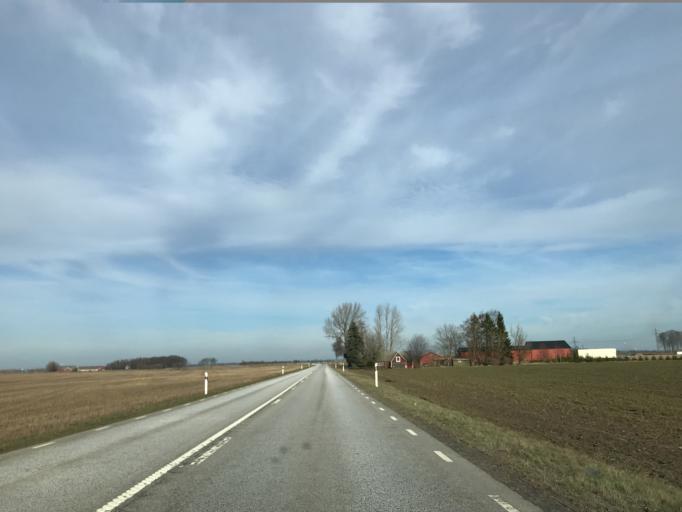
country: SE
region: Skane
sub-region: Tomelilla Kommun
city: Tomelilla
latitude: 55.5312
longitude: 13.9111
